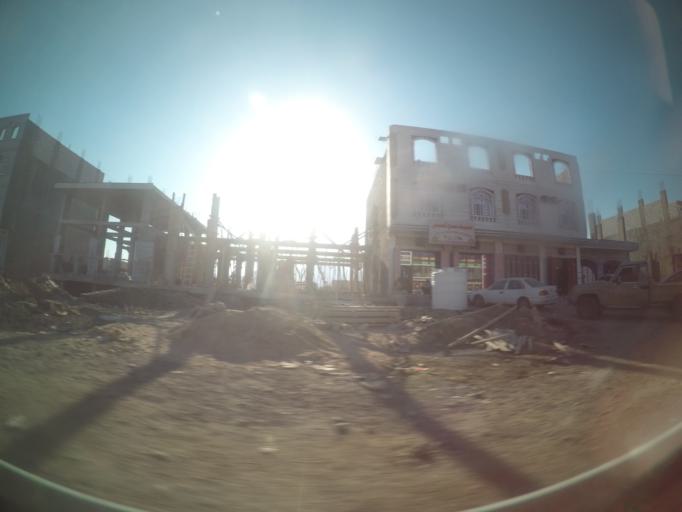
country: YE
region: Lahij
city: Habil ar Raydah
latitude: 13.6422
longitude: 44.8576
